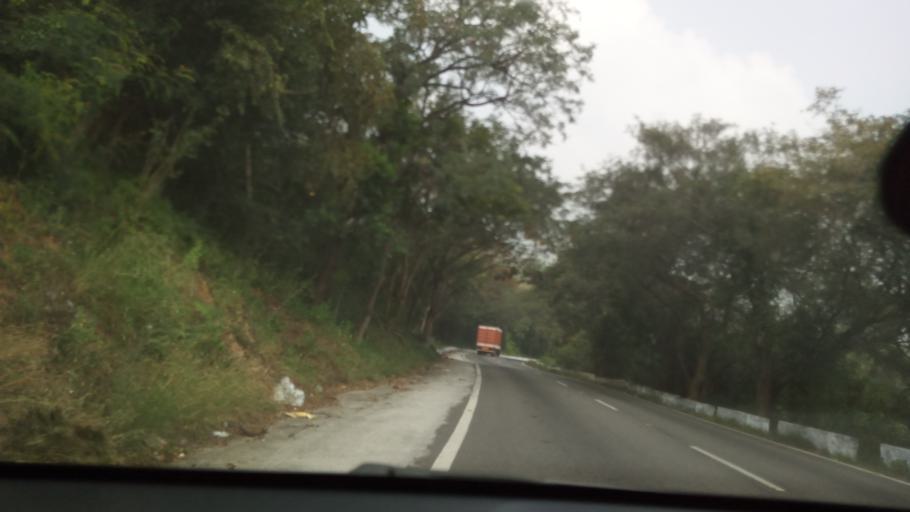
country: IN
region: Tamil Nadu
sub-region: Erode
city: Sathyamangalam
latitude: 11.5872
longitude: 77.1315
